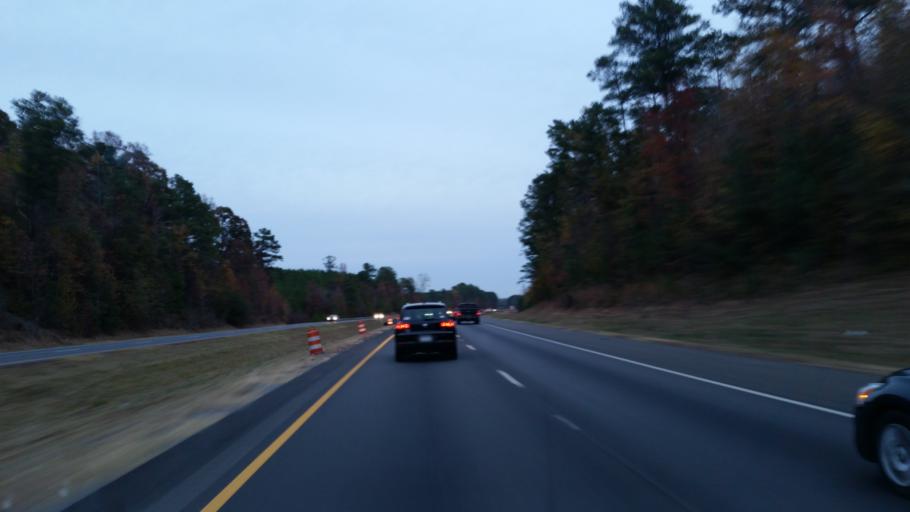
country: US
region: Alabama
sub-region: Greene County
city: Eutaw
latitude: 32.9014
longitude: -87.8922
